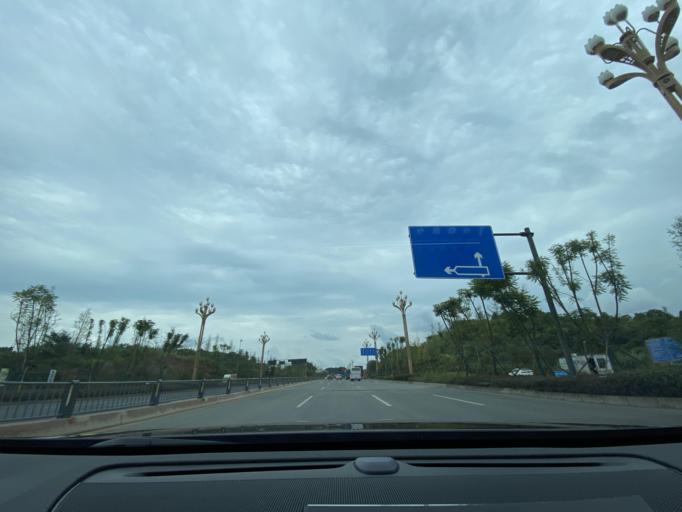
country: CN
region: Sichuan
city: Jiancheng
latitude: 30.4768
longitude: 104.4884
